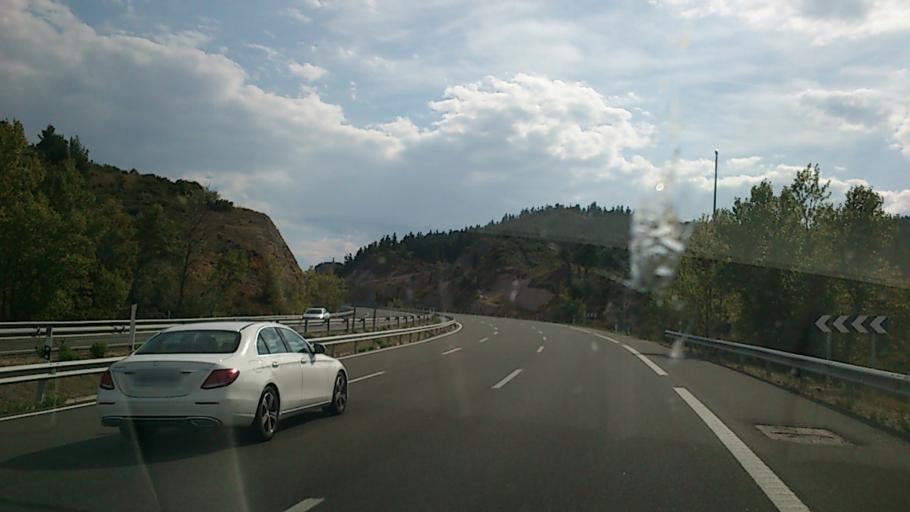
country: ES
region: La Rioja
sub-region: Provincia de La Rioja
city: Villalba de Rioja
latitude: 42.6263
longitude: -2.8566
